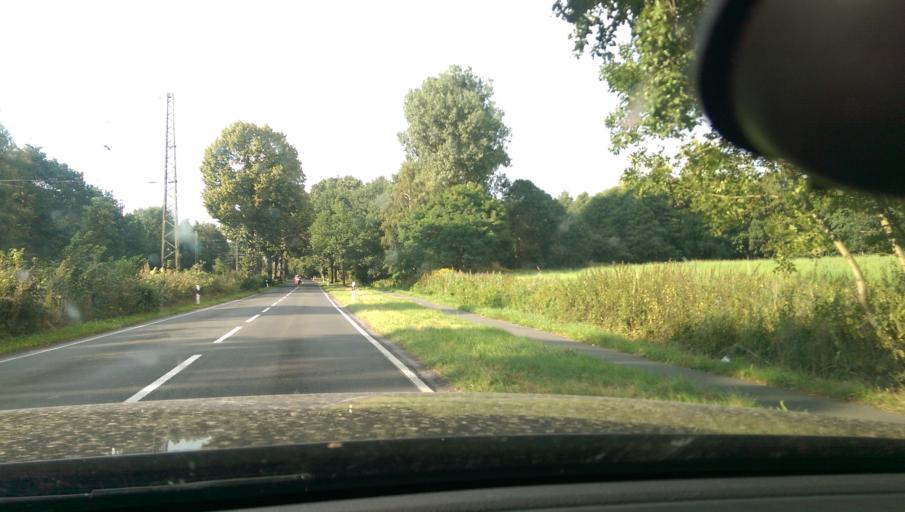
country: DE
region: Lower Saxony
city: Neustadt am Rubenberge
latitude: 52.4743
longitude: 9.4544
